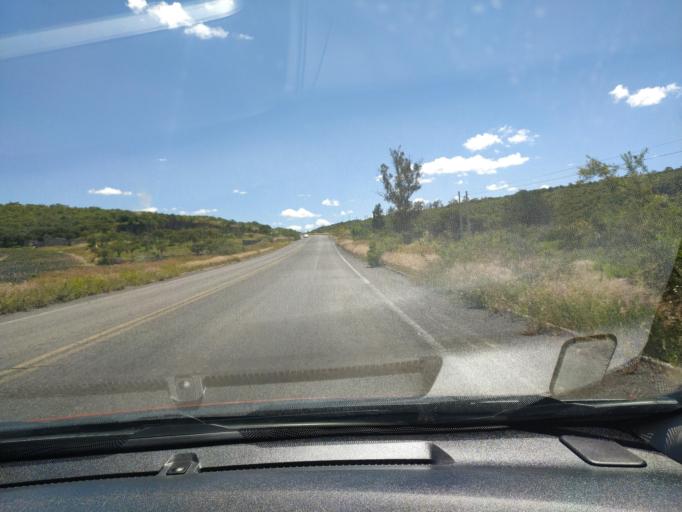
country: MX
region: Jalisco
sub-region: San Julian
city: Colonia Veintitres de Mayo
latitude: 21.0040
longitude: -102.2784
